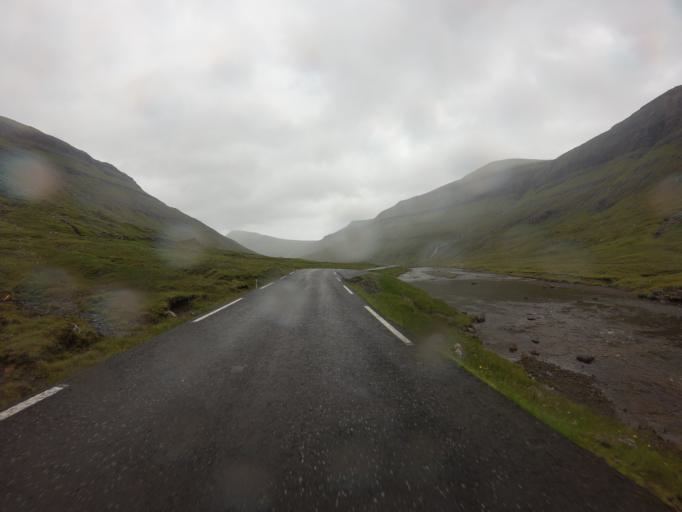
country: FO
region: Streymoy
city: Vestmanna
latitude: 62.2354
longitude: -7.1447
